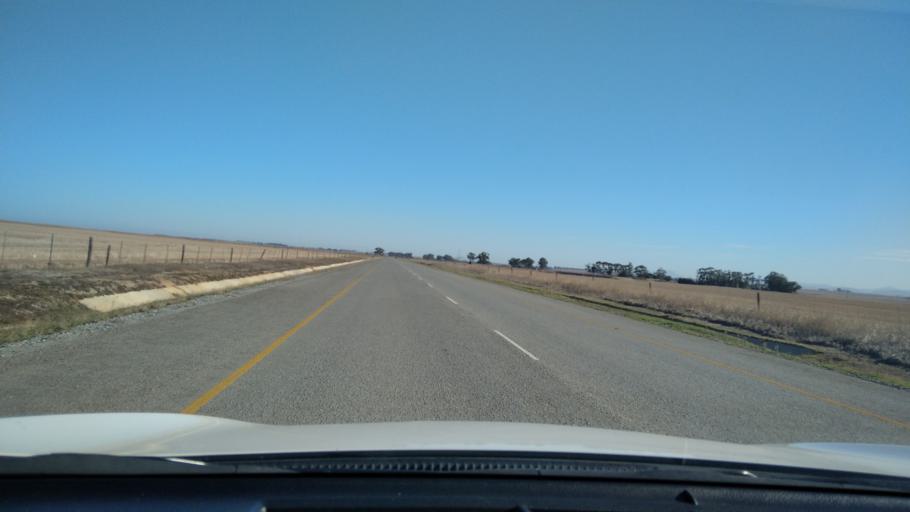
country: ZA
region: Western Cape
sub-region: West Coast District Municipality
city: Moorreesburg
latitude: -33.2934
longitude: 18.6101
